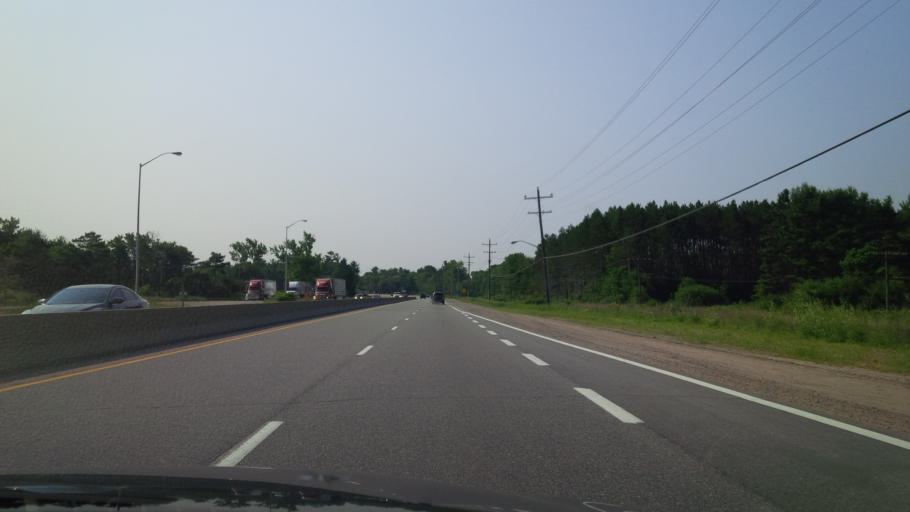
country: CA
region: Ontario
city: Gravenhurst
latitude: 44.9019
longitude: -79.3663
